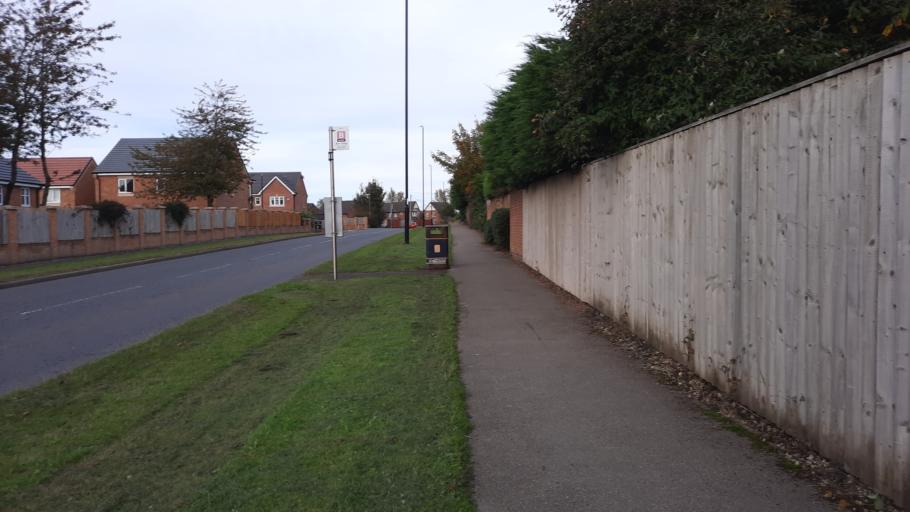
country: GB
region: England
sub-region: County Durham
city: Houghton-le-Spring
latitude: 54.8627
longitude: -1.4875
